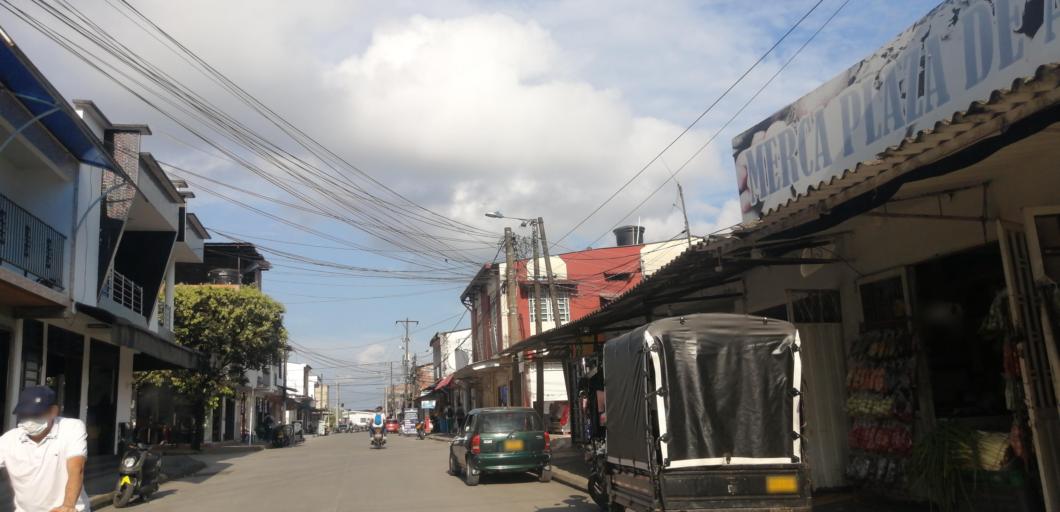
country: CO
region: Meta
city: Acacias
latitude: 3.9857
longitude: -73.7773
